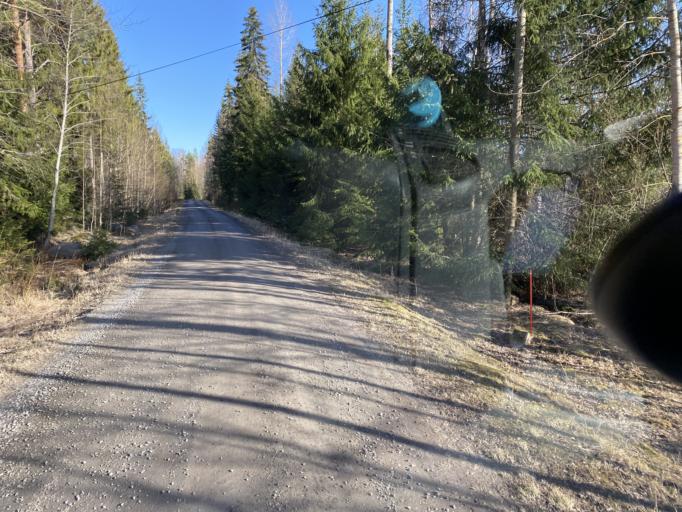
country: FI
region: Satakunta
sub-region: Rauma
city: Lappi
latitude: 61.1474
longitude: 21.9046
